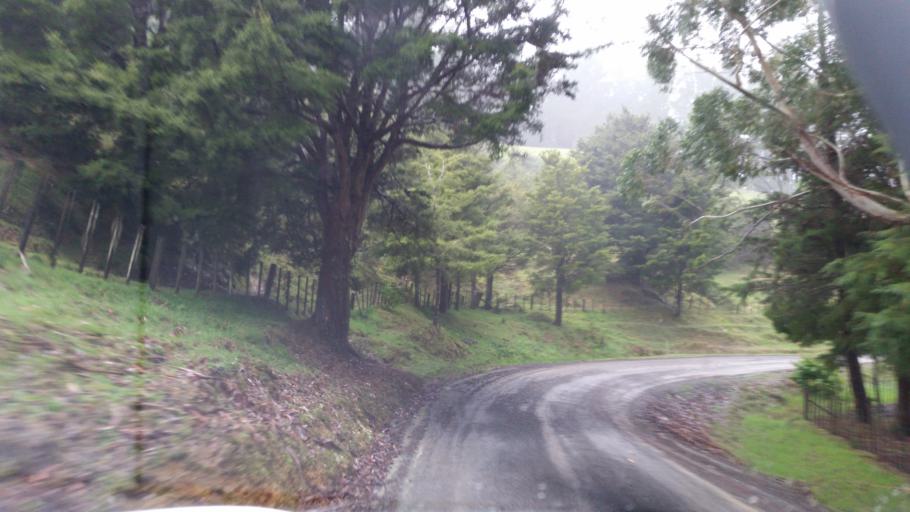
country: NZ
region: Northland
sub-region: Whangarei
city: Ngunguru
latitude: -35.4935
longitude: 174.4262
